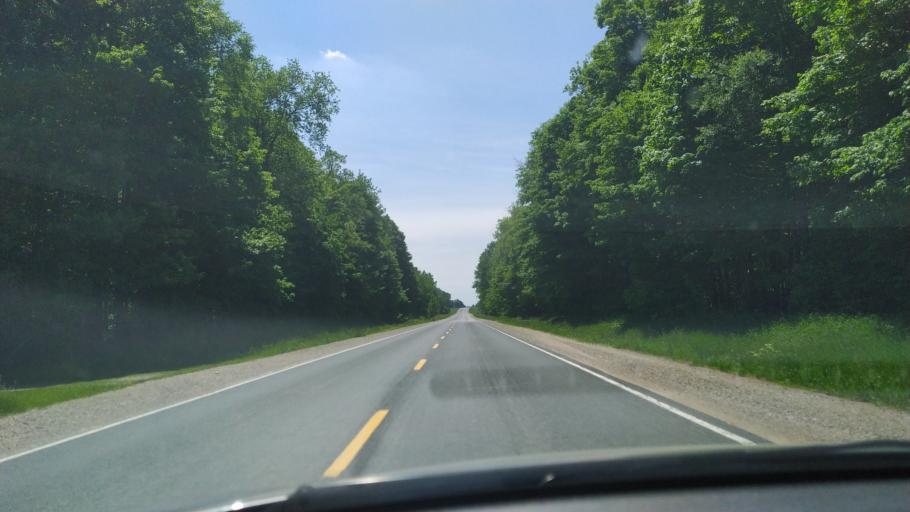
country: CA
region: Ontario
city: Ingersoll
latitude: 43.0451
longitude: -80.9806
